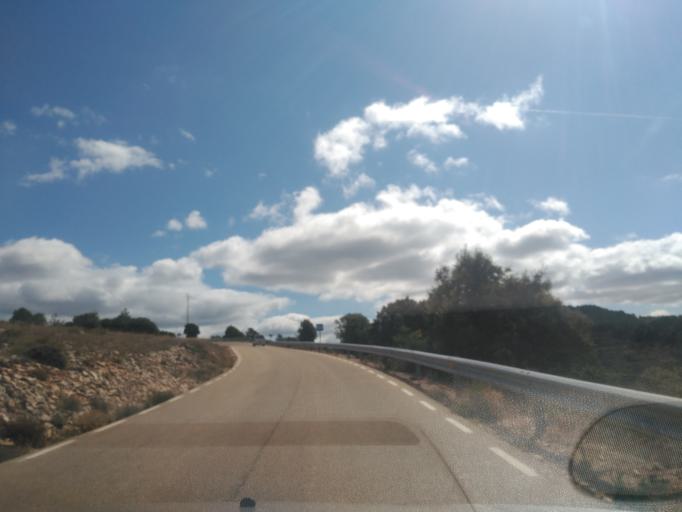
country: ES
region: Castille and Leon
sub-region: Provincia de Soria
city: Espejon
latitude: 41.8324
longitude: -3.2505
